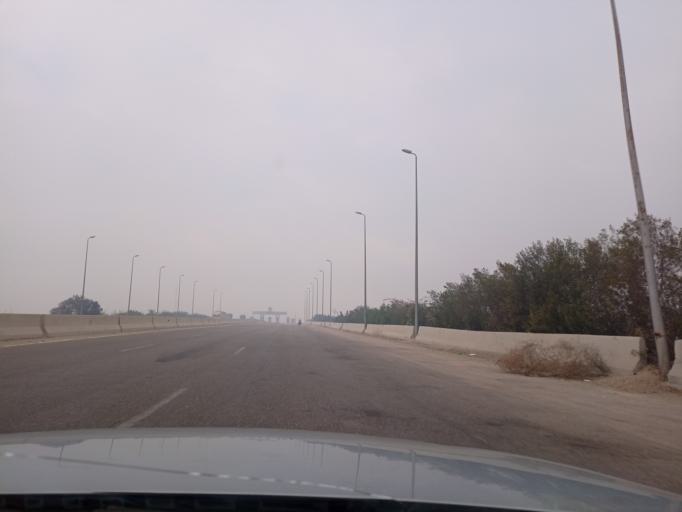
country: EG
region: Al Jizah
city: Al `Ayyat
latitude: 29.6834
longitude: 31.2289
